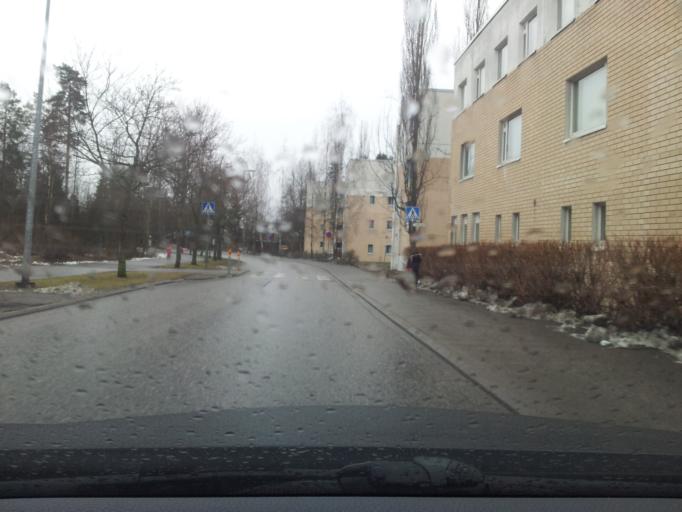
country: FI
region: Uusimaa
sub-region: Helsinki
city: Espoo
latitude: 60.1676
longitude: 24.6781
